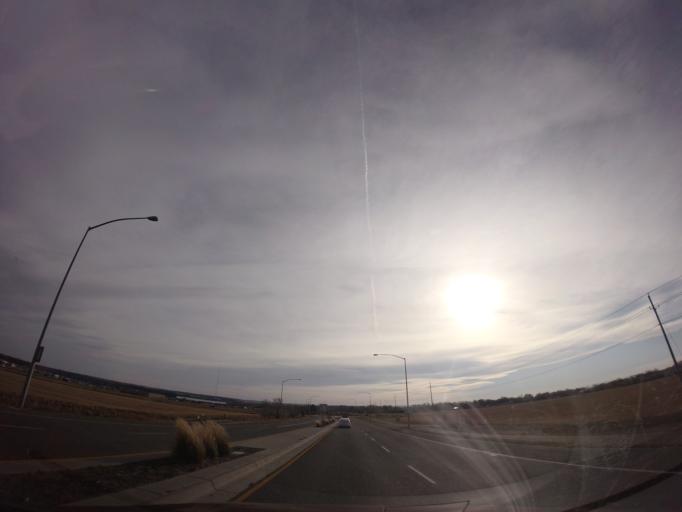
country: US
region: Montana
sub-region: Yellowstone County
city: Billings
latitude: 45.7377
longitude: -108.6175
